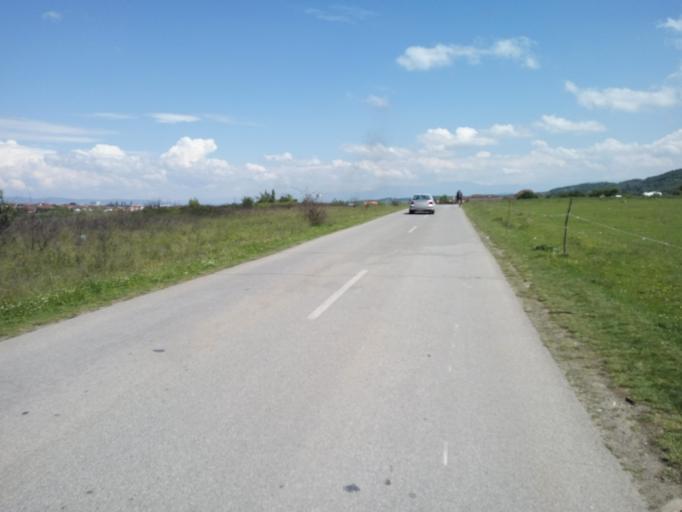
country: XK
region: Gjakova
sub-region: Komuna e Gjakoves
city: Gjakove
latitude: 42.3639
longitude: 20.4272
